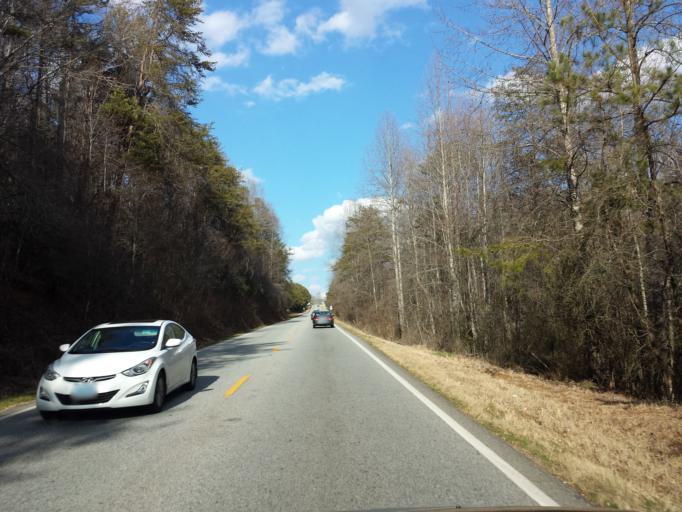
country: US
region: Georgia
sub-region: Lumpkin County
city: Dahlonega
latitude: 34.5172
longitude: -83.9198
